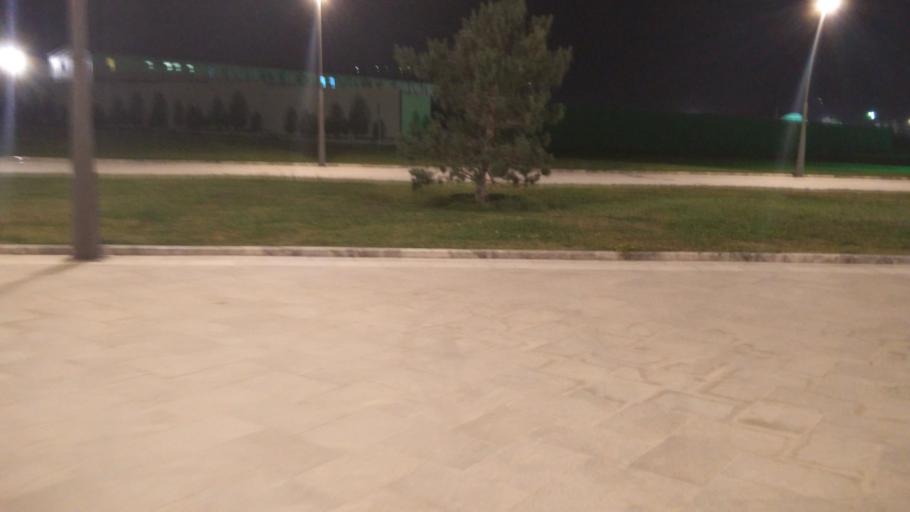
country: AZ
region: Baki
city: Baku
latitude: 40.3741
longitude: 49.8848
